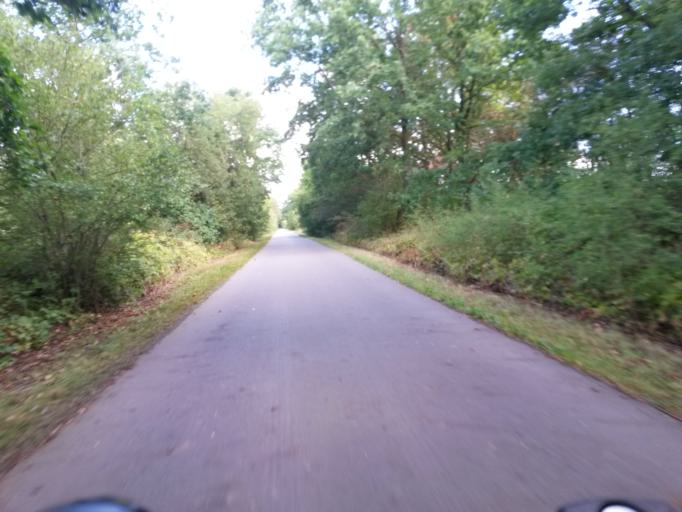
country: DE
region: Brandenburg
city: Templin
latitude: 53.2025
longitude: 13.5156
